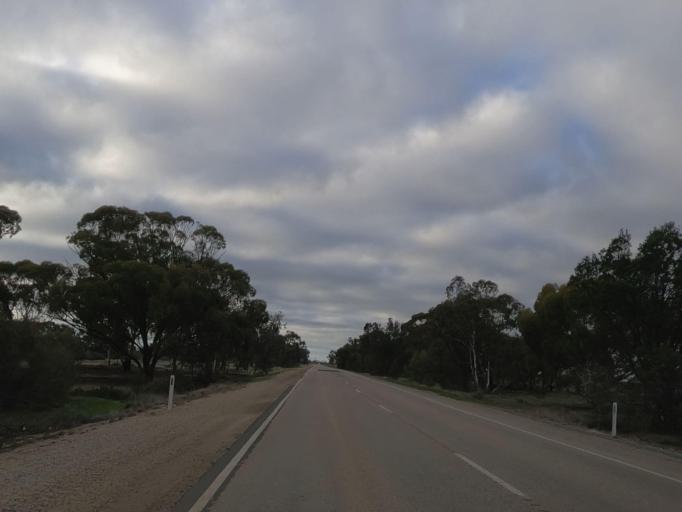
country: AU
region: Victoria
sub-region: Swan Hill
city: Swan Hill
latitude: -35.8197
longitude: 143.9510
